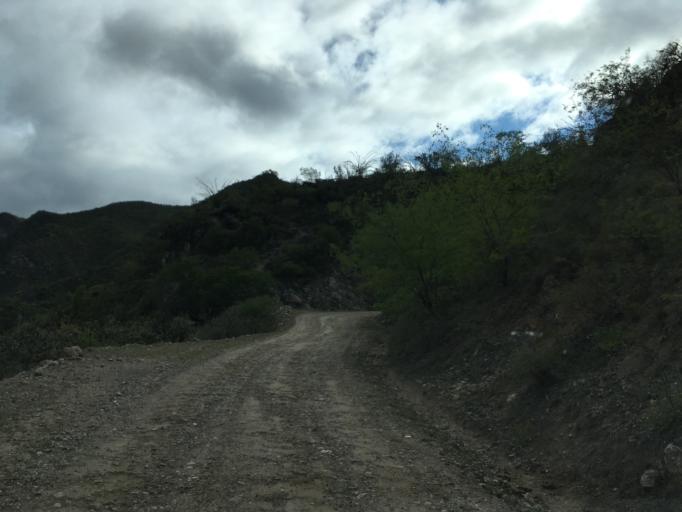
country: MX
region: Hidalgo
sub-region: Metztitlan
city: Fontezuelas
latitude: 20.6388
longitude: -98.9367
